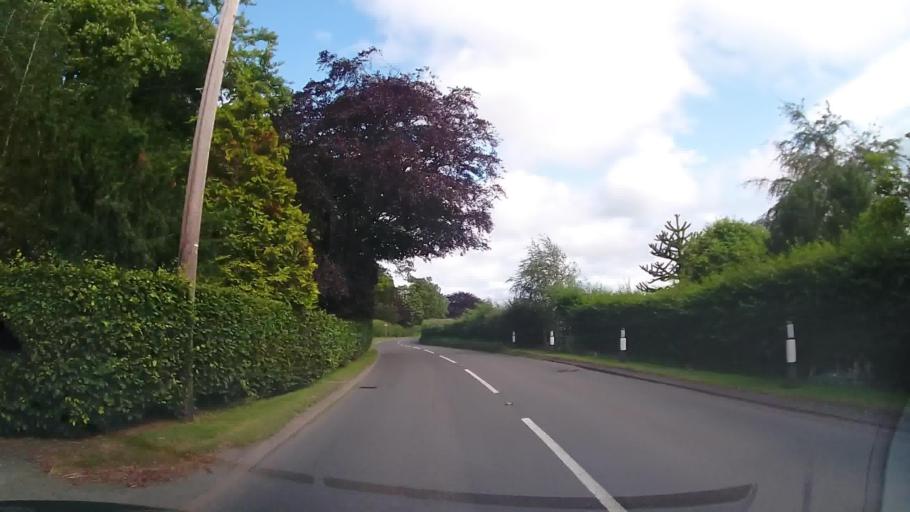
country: GB
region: England
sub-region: Shropshire
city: Pant
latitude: 52.7998
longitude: -3.0096
